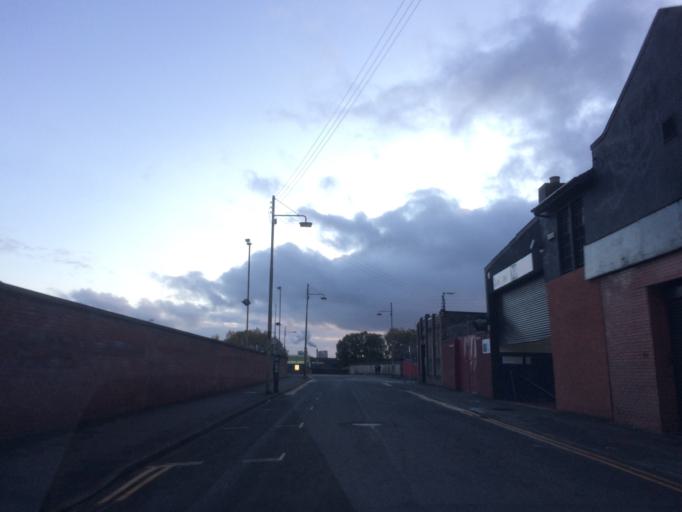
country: GB
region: Scotland
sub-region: Glasgow City
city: Glasgow
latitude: 55.8585
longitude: -4.2314
